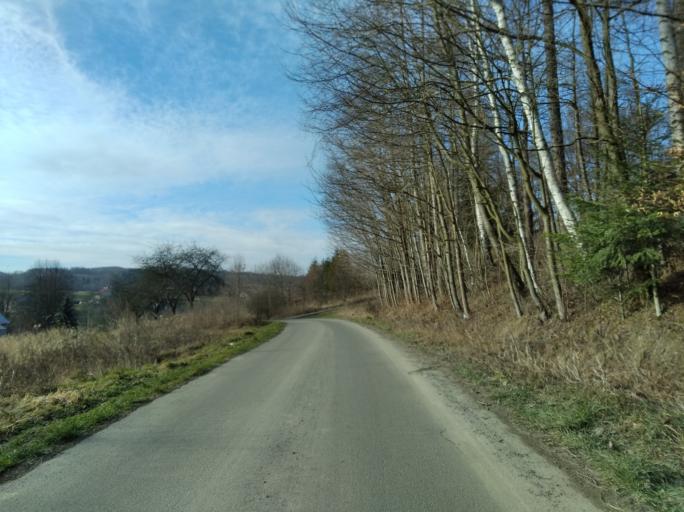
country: PL
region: Subcarpathian Voivodeship
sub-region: Powiat strzyzowski
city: Konieczkowa
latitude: 49.8310
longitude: 21.9364
